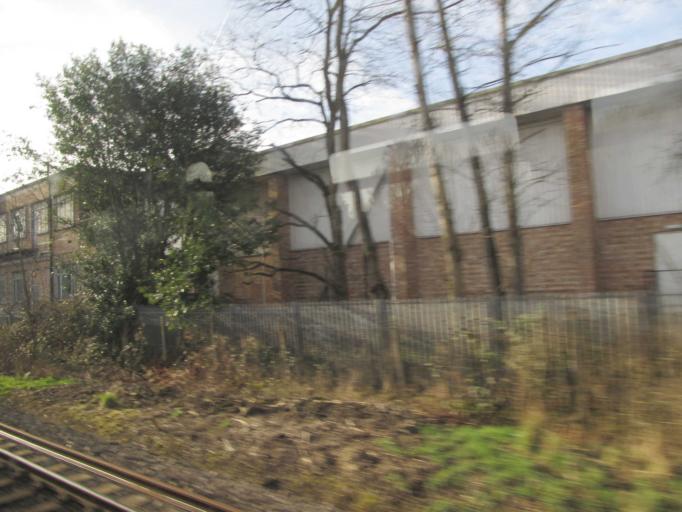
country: GB
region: England
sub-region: Surrey
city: Frimley
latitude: 51.3135
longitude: -0.7567
